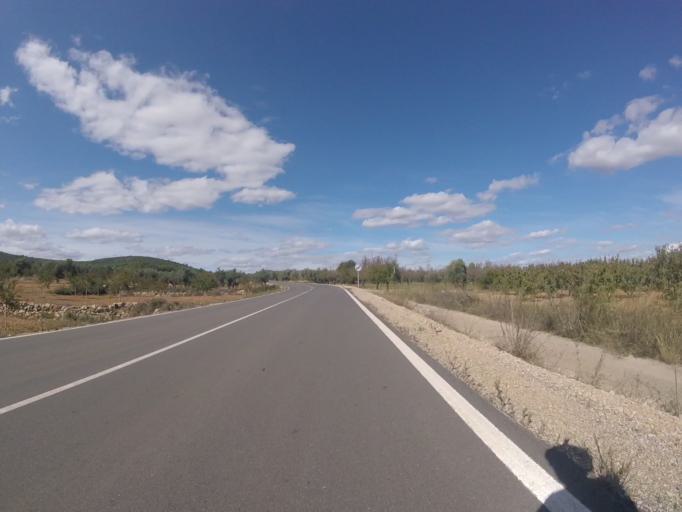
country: ES
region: Valencia
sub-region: Provincia de Castello
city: Chert/Xert
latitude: 40.4293
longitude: 0.1420
